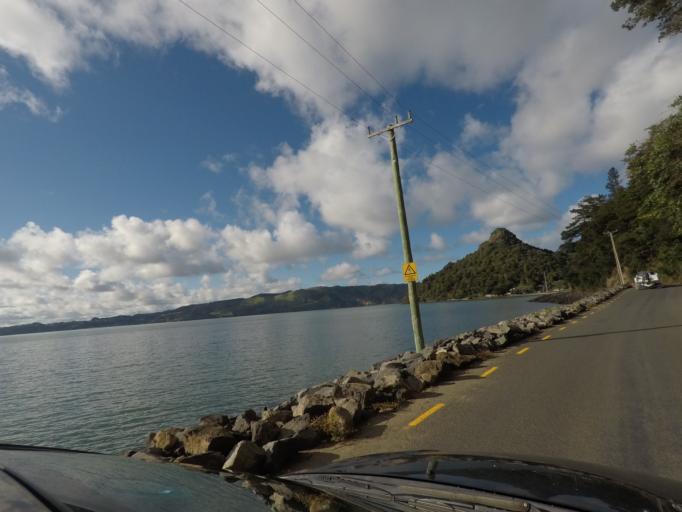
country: NZ
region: Auckland
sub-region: Auckland
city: Titirangi
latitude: -37.0121
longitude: 174.5614
